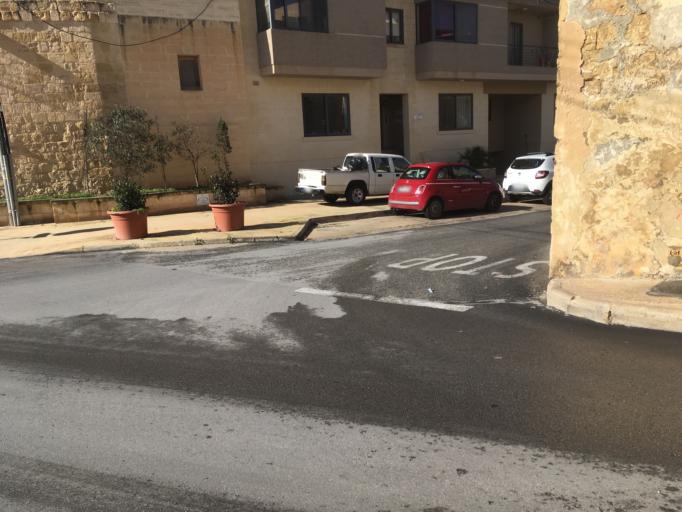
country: MT
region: Il-Mosta
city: Mosta
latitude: 35.9104
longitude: 14.4313
